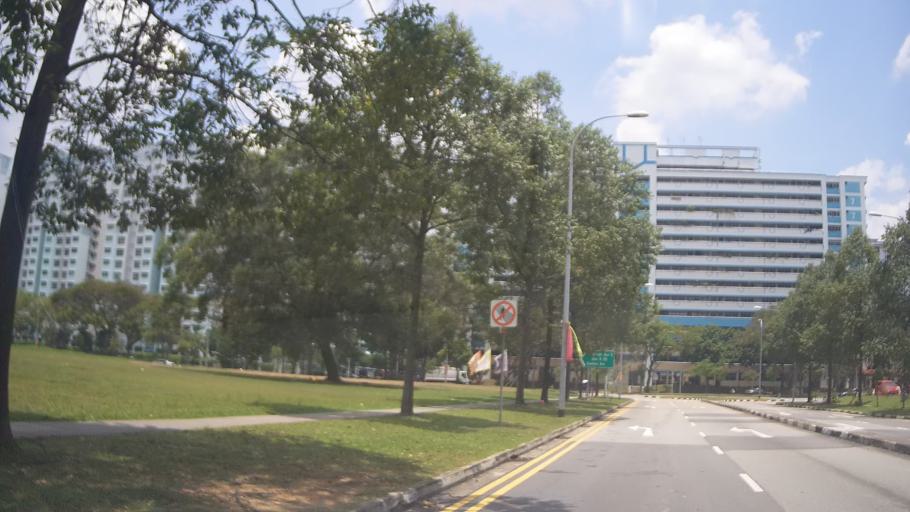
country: MY
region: Johor
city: Johor Bahru
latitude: 1.4498
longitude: 103.7991
